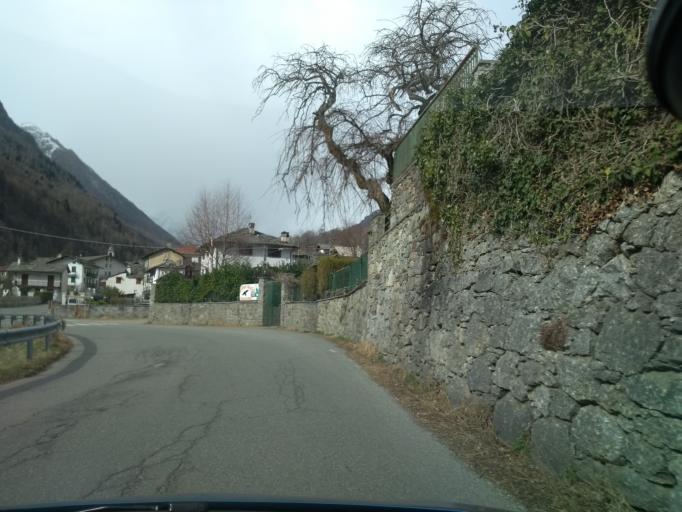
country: IT
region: Piedmont
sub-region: Provincia di Torino
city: Chialamberto
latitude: 45.3672
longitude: 7.3256
